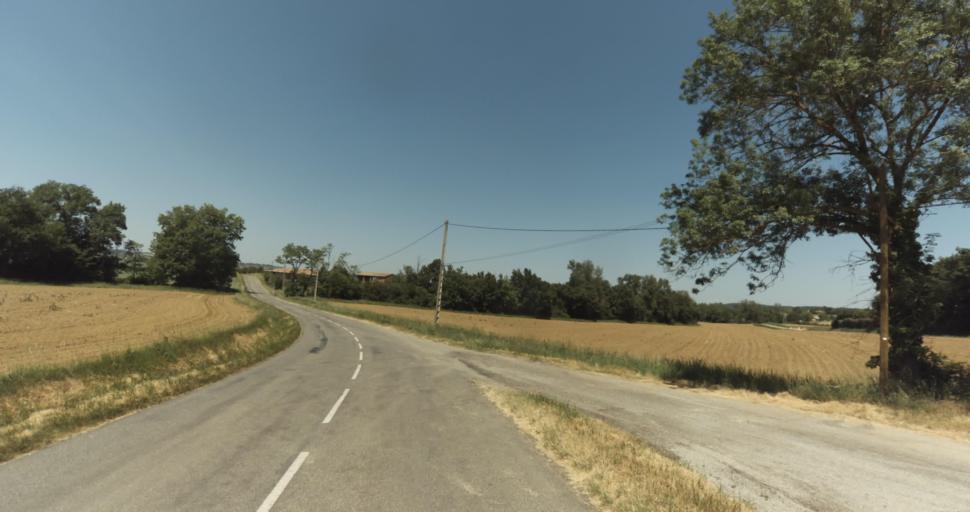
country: FR
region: Midi-Pyrenees
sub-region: Departement du Gers
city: Pujaudran
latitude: 43.6310
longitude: 1.1565
